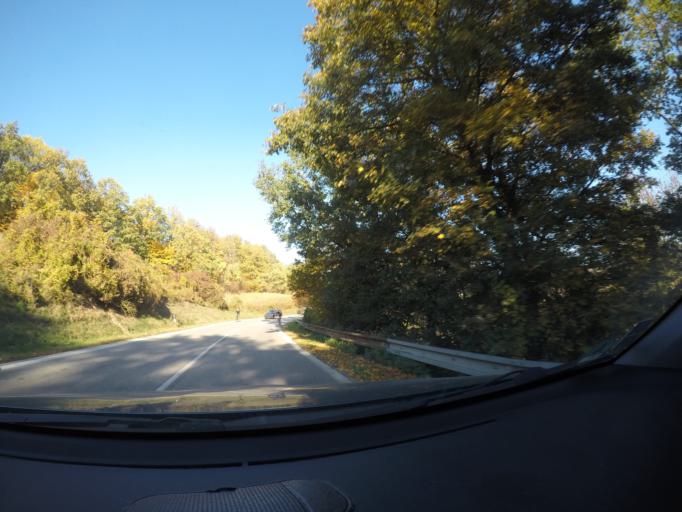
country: SK
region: Trenciansky
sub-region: Okres Trencin
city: Trencin
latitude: 48.9053
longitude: 18.0711
